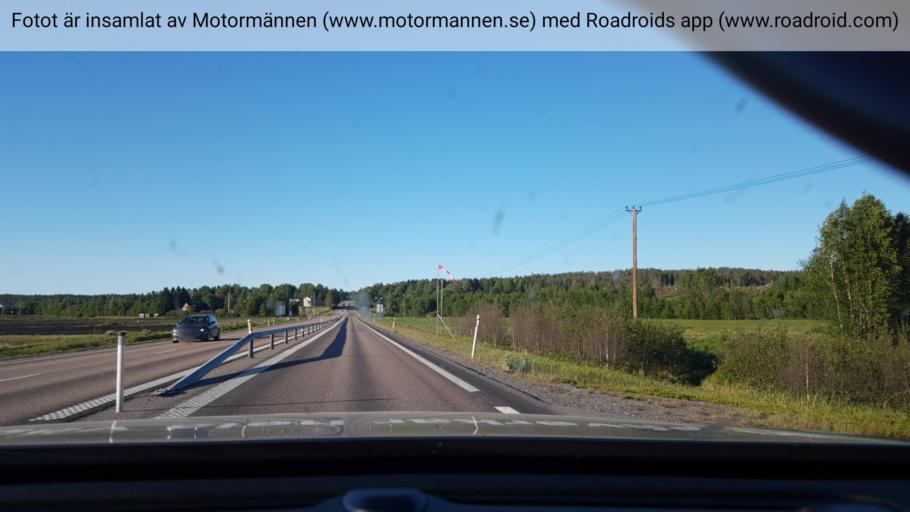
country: SE
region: Vaesternorrland
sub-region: OErnskoeldsviks Kommun
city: Husum
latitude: 63.3271
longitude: 19.0534
